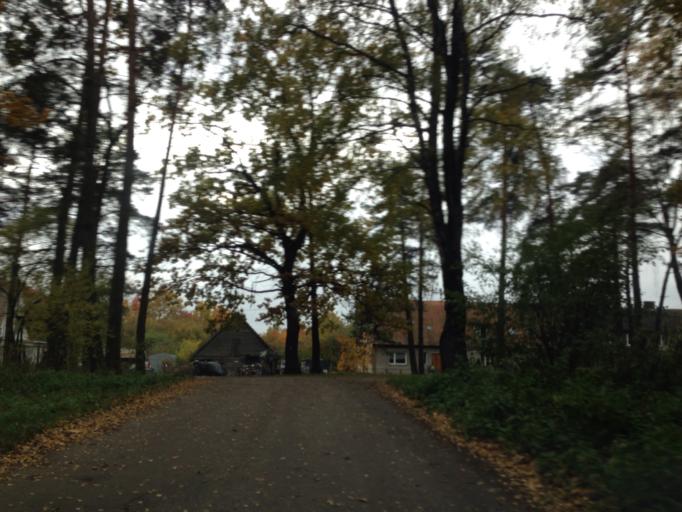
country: PL
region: Pomeranian Voivodeship
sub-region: Powiat kwidzynski
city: Prabuty
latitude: 53.7343
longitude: 19.2101
